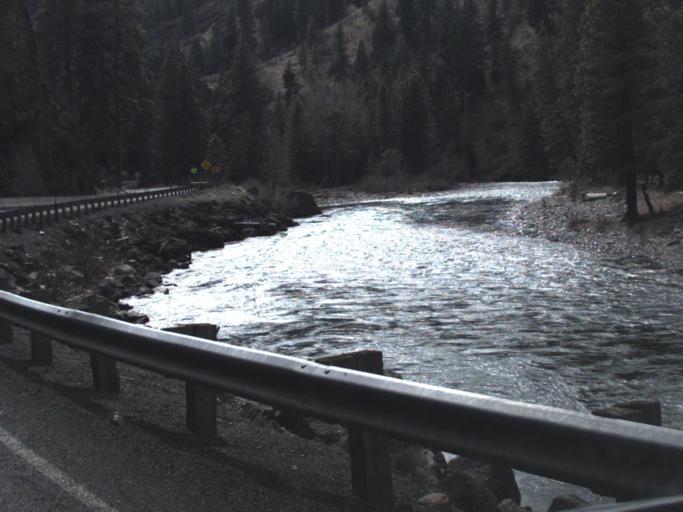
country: US
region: Washington
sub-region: Yakima County
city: Tieton
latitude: 46.8882
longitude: -120.9871
